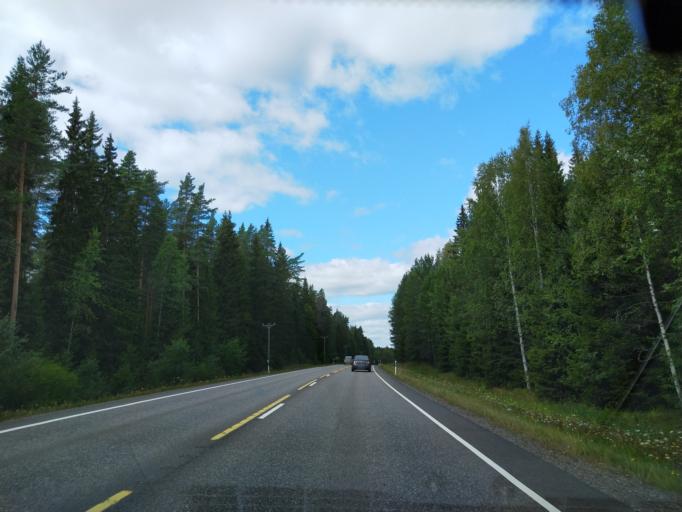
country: FI
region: Haeme
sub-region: Riihimaeki
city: Loppi
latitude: 60.7513
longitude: 24.3113
